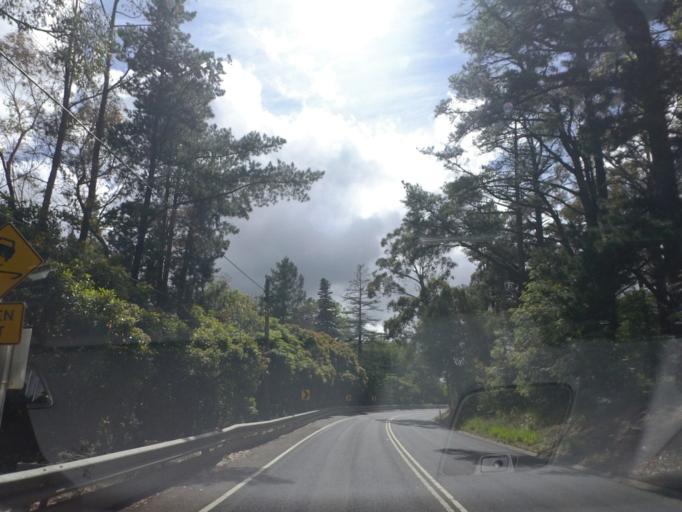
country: AU
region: Victoria
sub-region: Cardinia
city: Emerald
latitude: -37.9257
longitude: 145.4487
